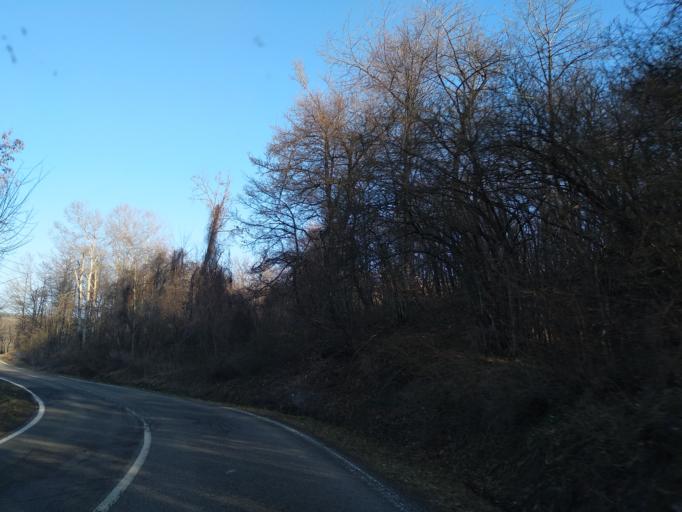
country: IT
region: Emilia-Romagna
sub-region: Provincia di Reggio Emilia
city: Ramiseto
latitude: 44.4082
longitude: 10.3096
